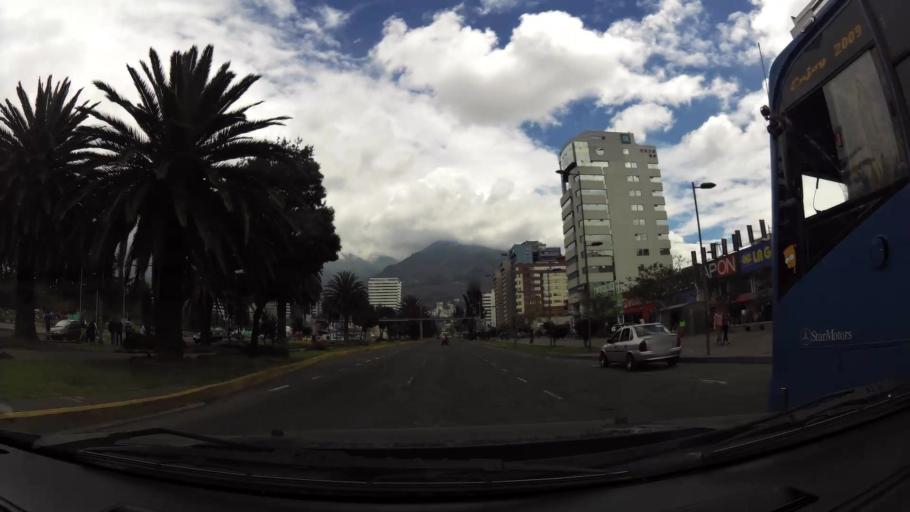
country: EC
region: Pichincha
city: Quito
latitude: -0.1764
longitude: -78.4821
